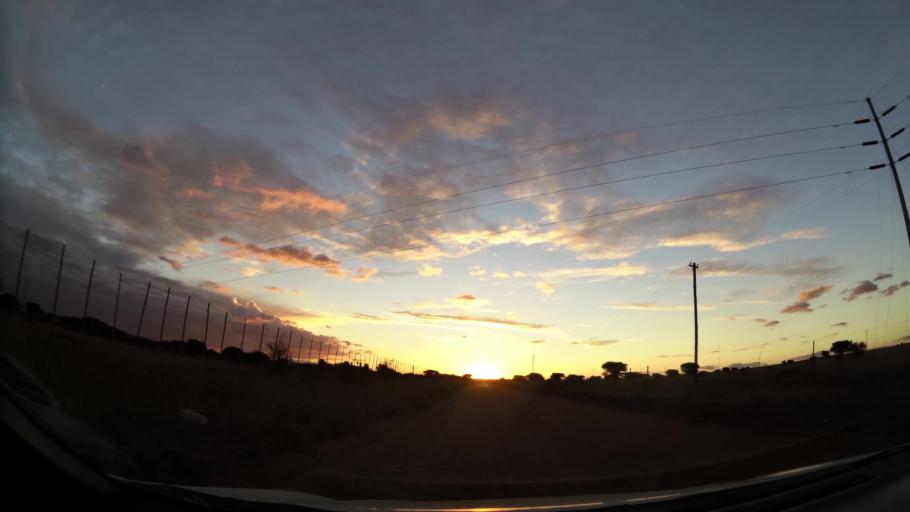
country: ZA
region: Limpopo
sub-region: Capricorn District Municipality
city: Polokwane
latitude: -23.7410
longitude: 29.4535
